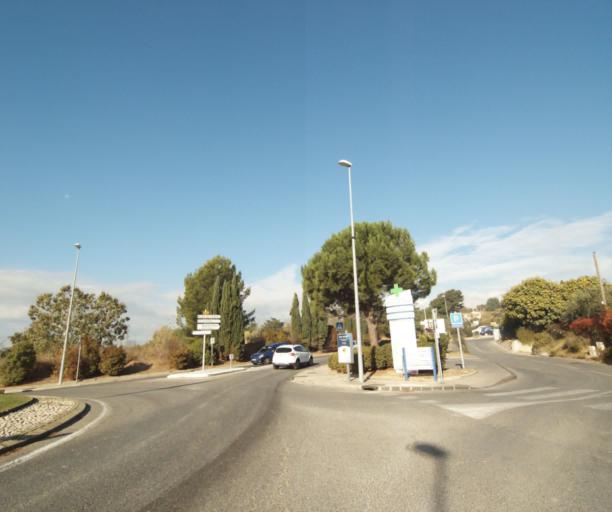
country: FR
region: Provence-Alpes-Cote d'Azur
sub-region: Departement des Bouches-du-Rhone
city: Allauch
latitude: 43.3220
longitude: 5.4932
